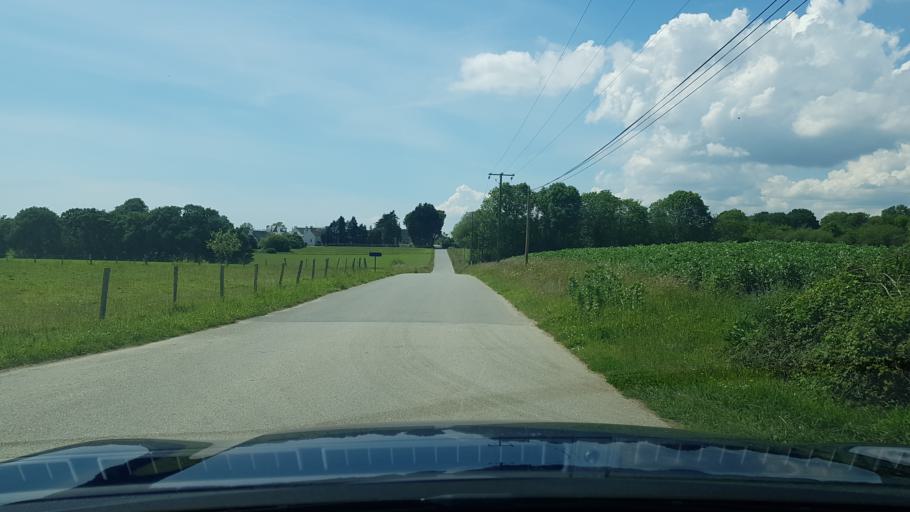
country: FR
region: Brittany
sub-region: Departement du Finistere
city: Clohars-Carnoet
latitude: 47.7929
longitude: -3.5759
